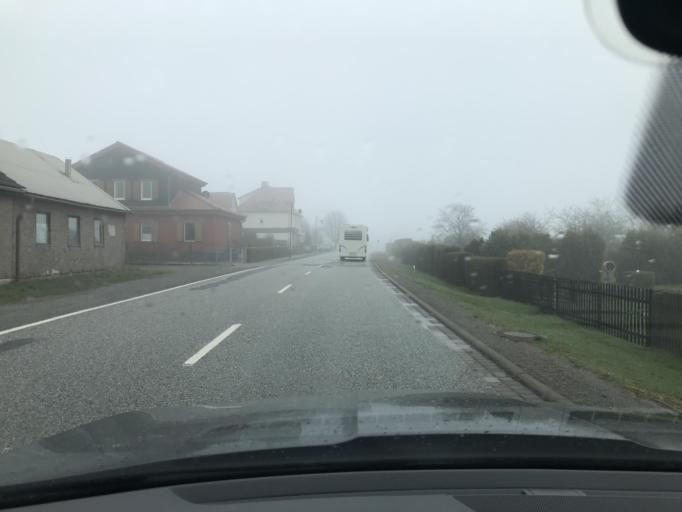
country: DE
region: Saxony-Anhalt
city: Harzgerode
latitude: 51.6509
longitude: 11.1392
